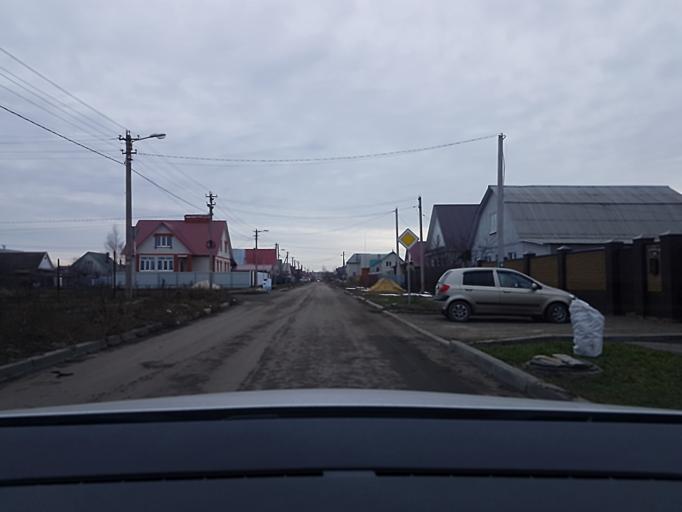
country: RU
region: Tambov
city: Tambov
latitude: 52.7825
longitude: 41.3767
